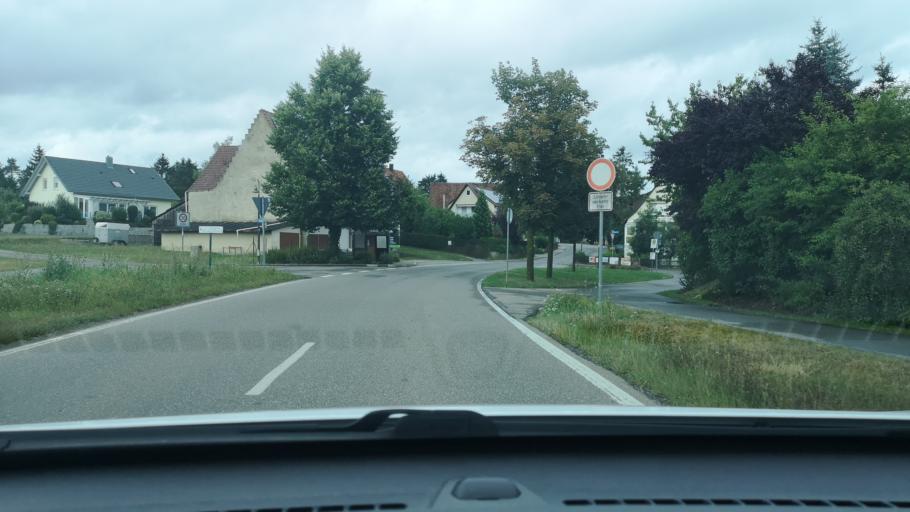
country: DE
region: Baden-Wuerttemberg
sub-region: Freiburg Region
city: Vohringen
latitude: 48.3324
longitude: 8.6566
